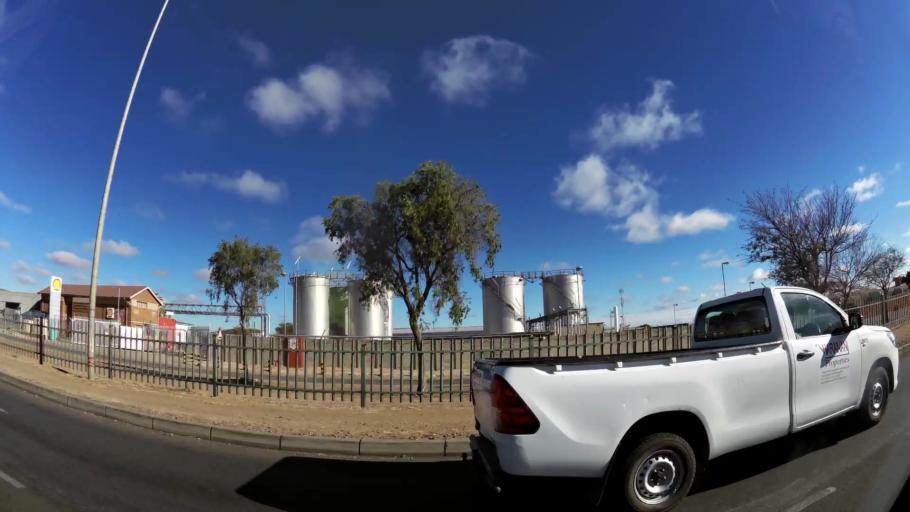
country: ZA
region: Limpopo
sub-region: Capricorn District Municipality
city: Polokwane
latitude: -23.8888
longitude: 29.4545
